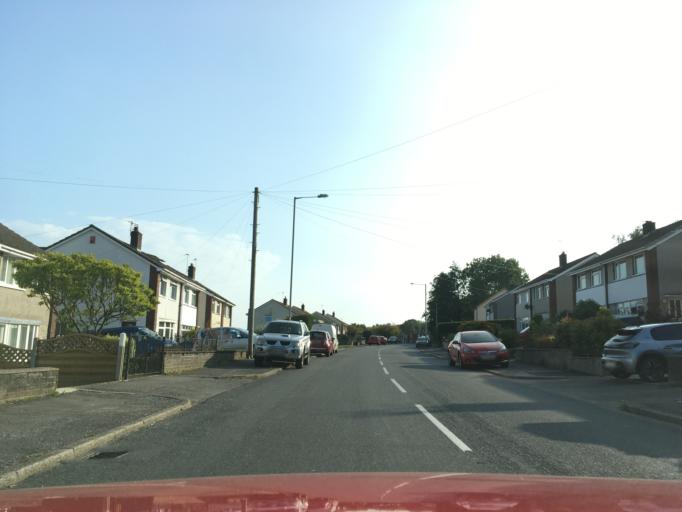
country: GB
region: Wales
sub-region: Torfaen County Borough
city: Cwmbran
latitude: 51.6637
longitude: -3.0457
